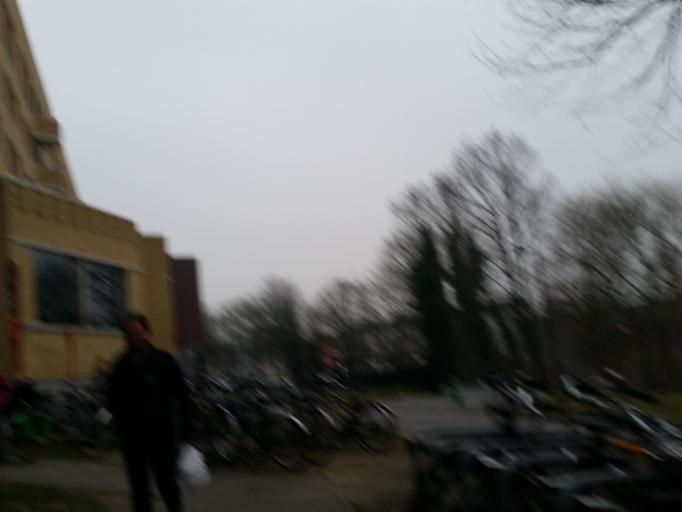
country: BE
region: Flanders
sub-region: Provincie Oost-Vlaanderen
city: Ledeberg
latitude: 51.0395
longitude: 3.7288
